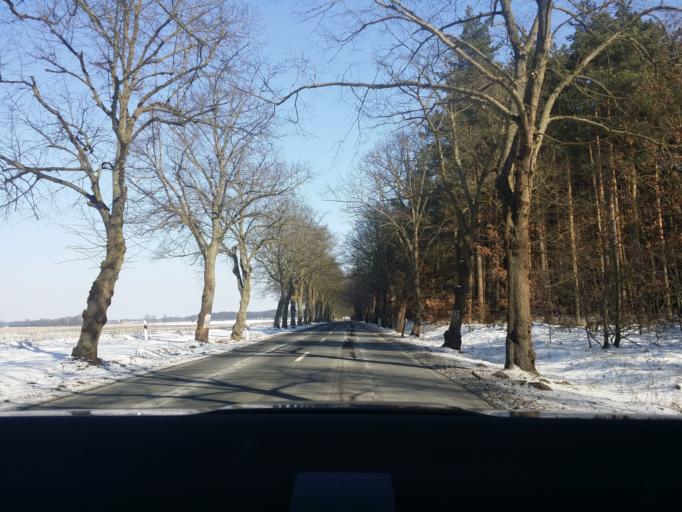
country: DE
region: Brandenburg
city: Wittstock
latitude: 53.1982
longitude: 12.5700
